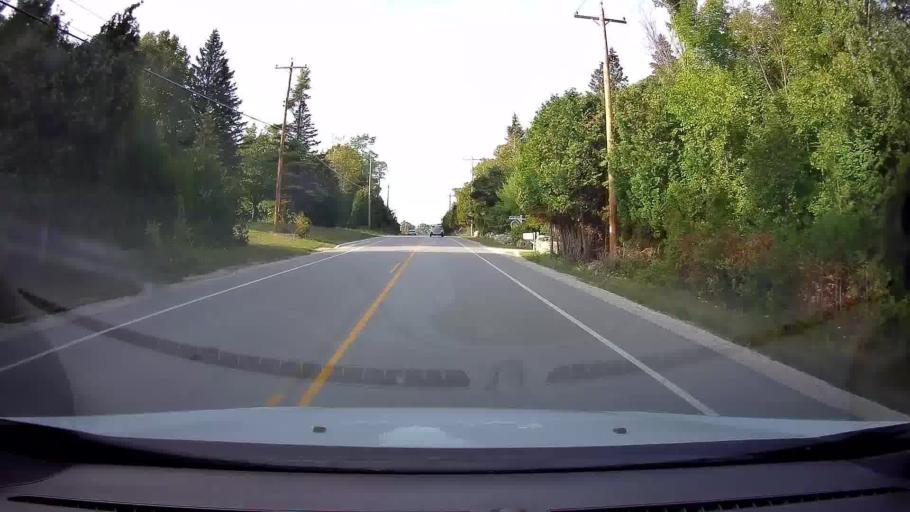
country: US
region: Wisconsin
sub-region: Door County
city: Sturgeon Bay
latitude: 45.1642
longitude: -87.1323
